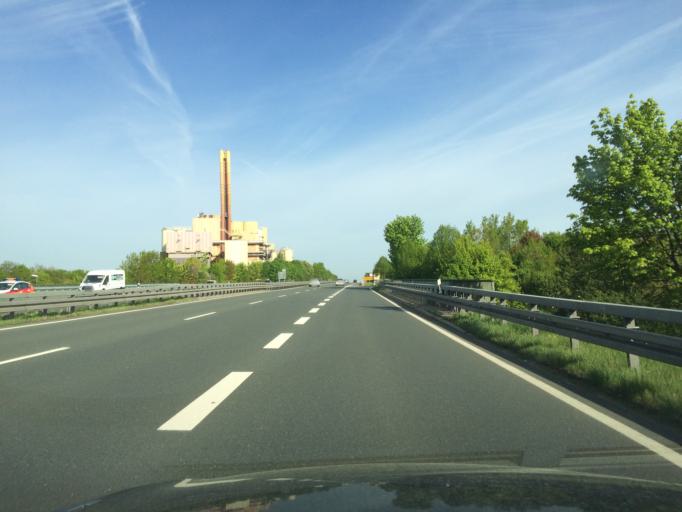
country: DE
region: Bavaria
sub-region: Regierungsbezirk Unterfranken
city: Gerbrunn
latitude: 49.7907
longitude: 9.9991
